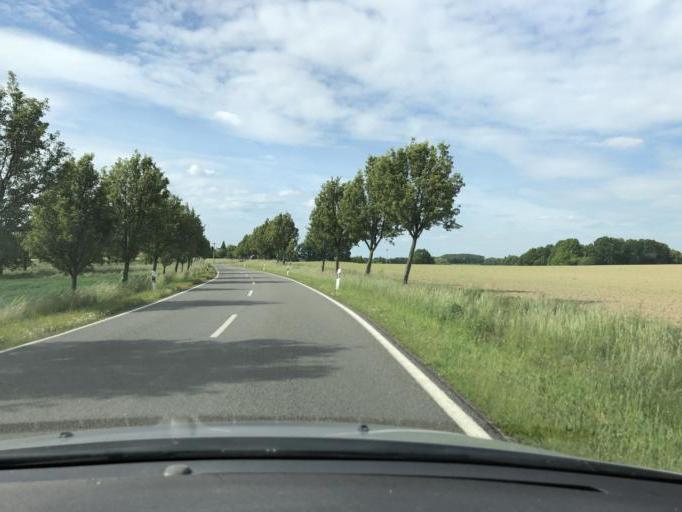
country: DE
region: Saxony
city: Nerchau
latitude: 51.2250
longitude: 12.8012
